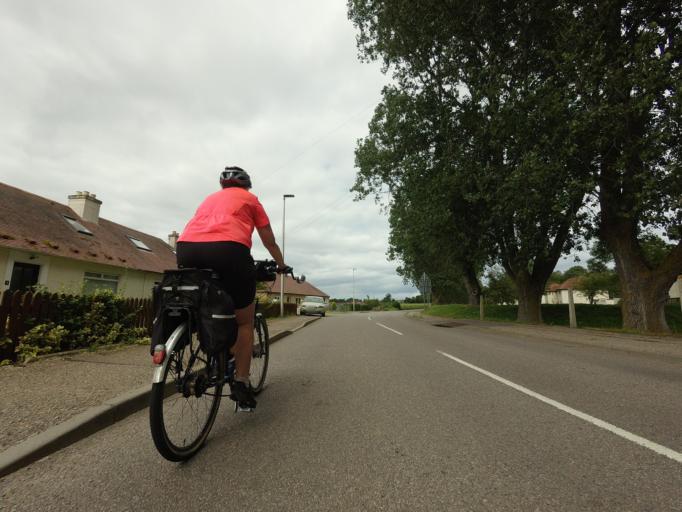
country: GB
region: Scotland
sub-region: Moray
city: Kinloss
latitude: 57.6322
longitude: -3.5600
